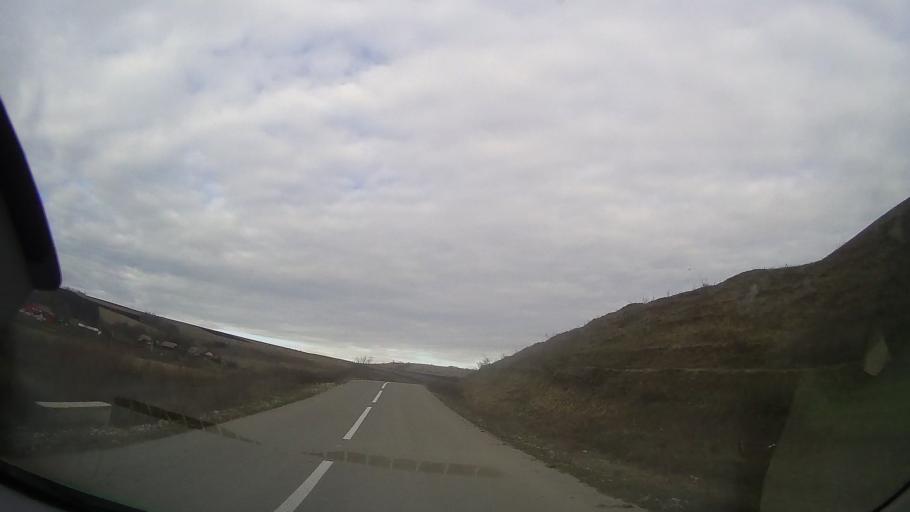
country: RO
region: Bistrita-Nasaud
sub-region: Comuna Silvasu de Campie
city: Silvasu de Campie
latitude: 46.7868
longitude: 24.2861
